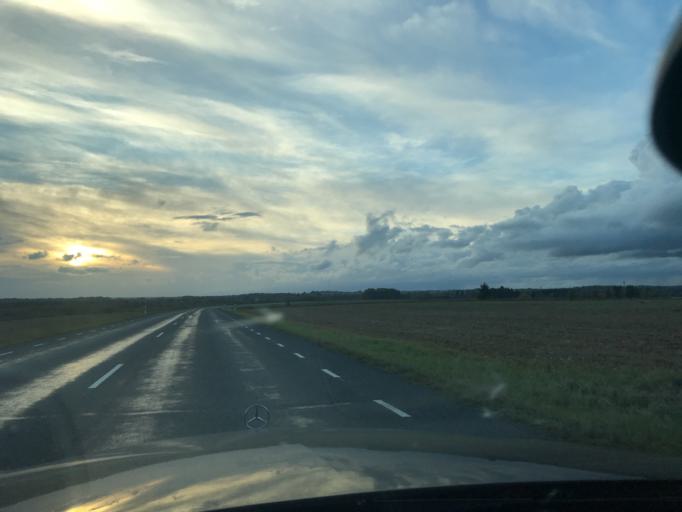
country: EE
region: Vorumaa
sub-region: Antsla vald
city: Vana-Antsla
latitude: 57.9162
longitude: 26.3603
